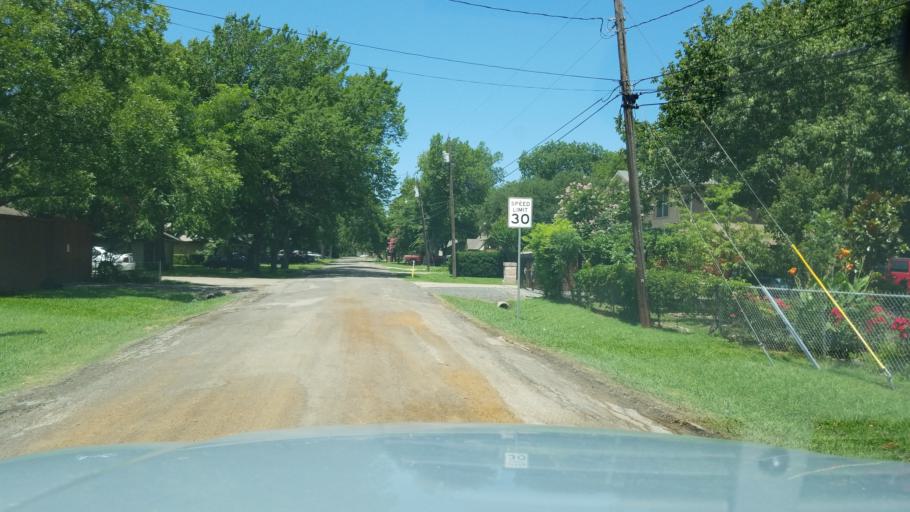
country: US
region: Texas
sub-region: Dallas County
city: Irving
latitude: 32.8022
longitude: -96.9259
